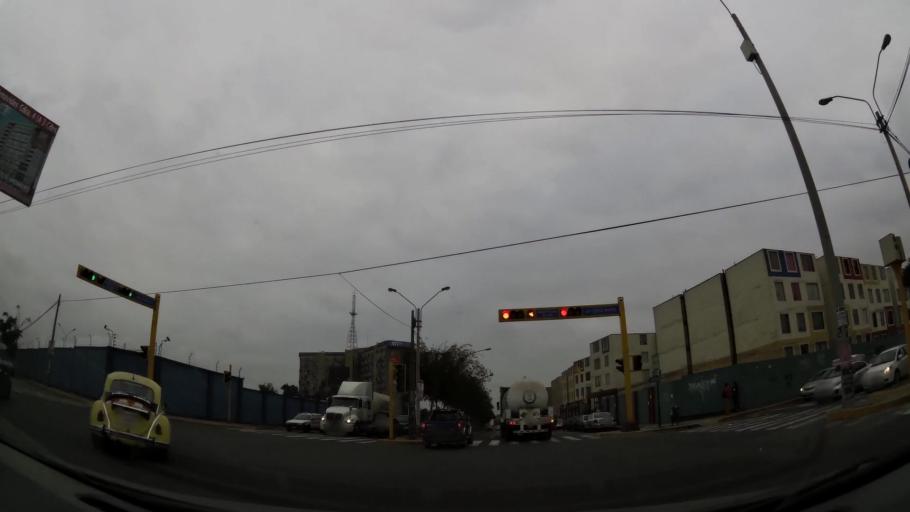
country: PE
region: Lima
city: Lima
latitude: -12.0490
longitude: -77.0538
